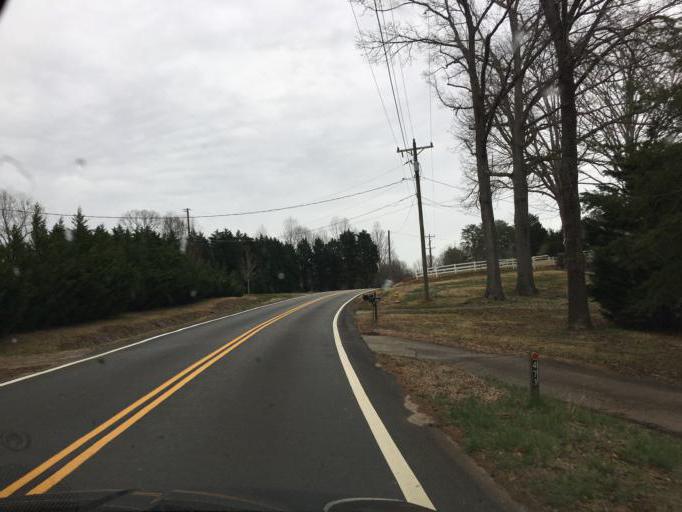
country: US
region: South Carolina
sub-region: Greenville County
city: Berea
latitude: 34.9303
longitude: -82.4950
